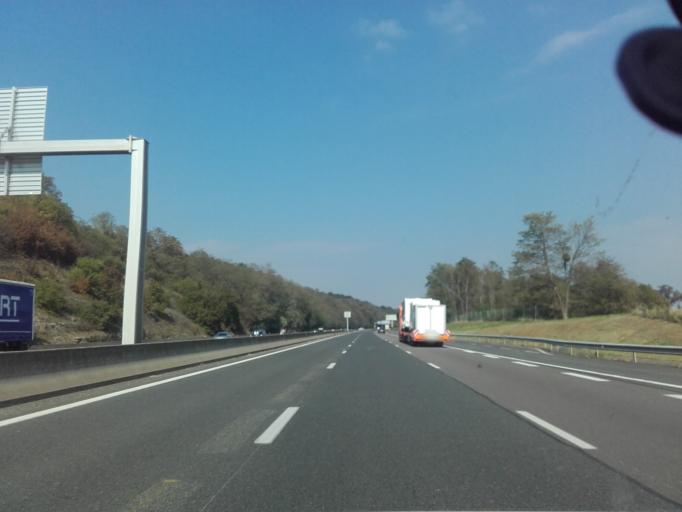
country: FR
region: Bourgogne
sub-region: Departement de Saone-et-Loire
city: Sance
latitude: 46.3570
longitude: 4.8290
